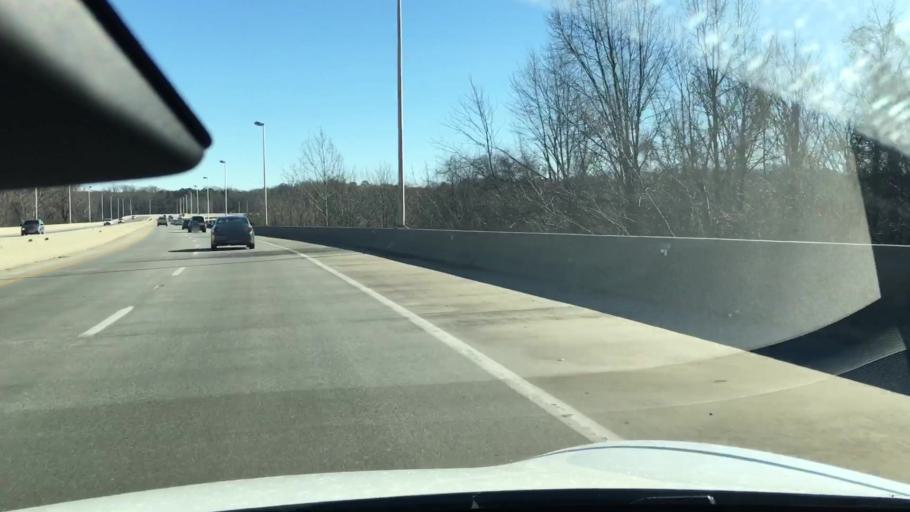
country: US
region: Virginia
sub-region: Henrico County
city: Tuckahoe
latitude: 37.5627
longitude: -77.5758
